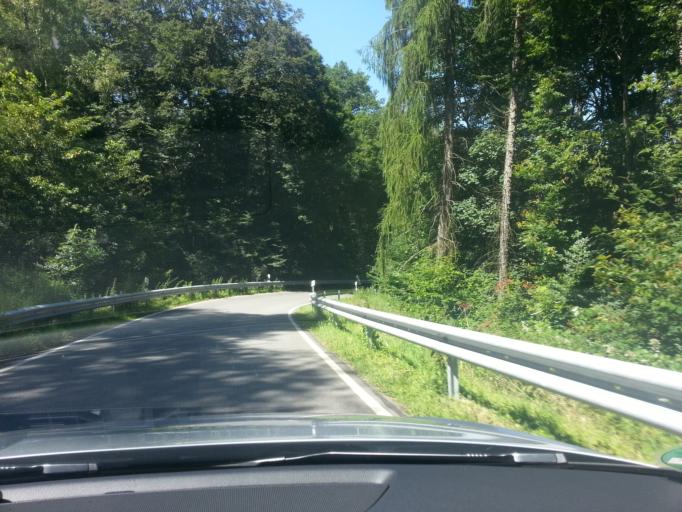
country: DE
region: Rheinland-Pfalz
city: Fockelberg
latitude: 49.5383
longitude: 7.4858
